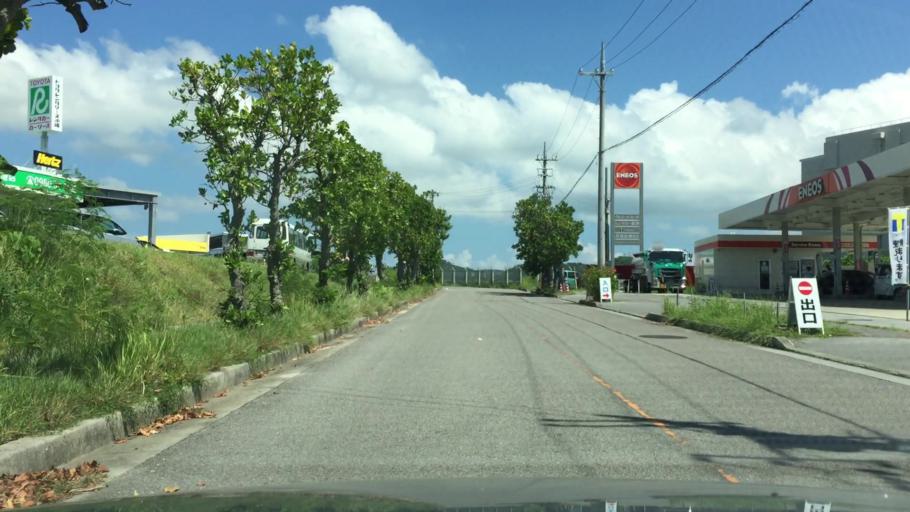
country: JP
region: Okinawa
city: Ishigaki
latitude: 24.3883
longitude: 124.2434
